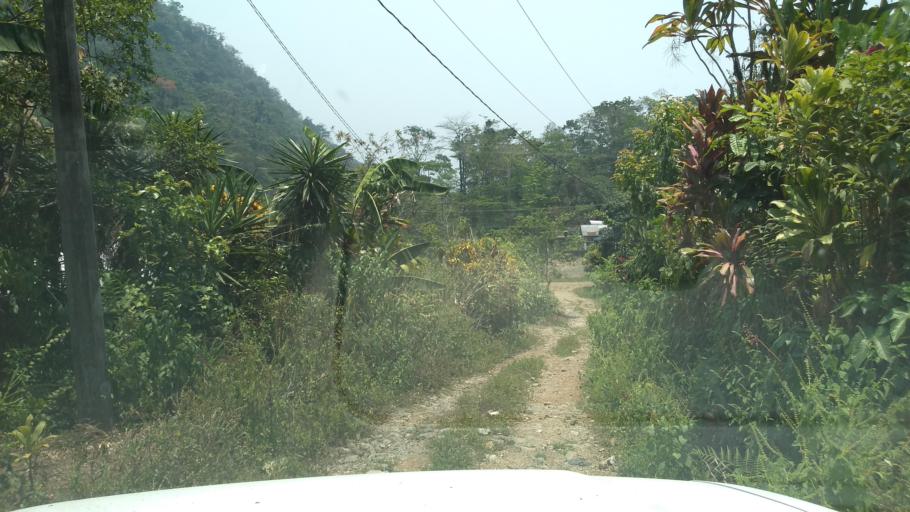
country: MX
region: Veracruz
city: Motzorongo
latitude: 18.6002
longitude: -96.7472
